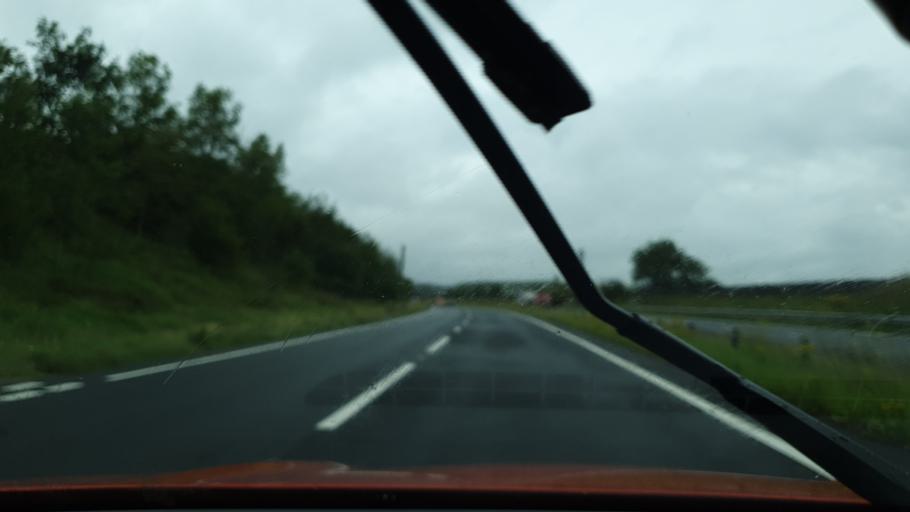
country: GB
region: England
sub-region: Cumbria
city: Grange-over-Sands
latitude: 54.2311
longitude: -2.9149
